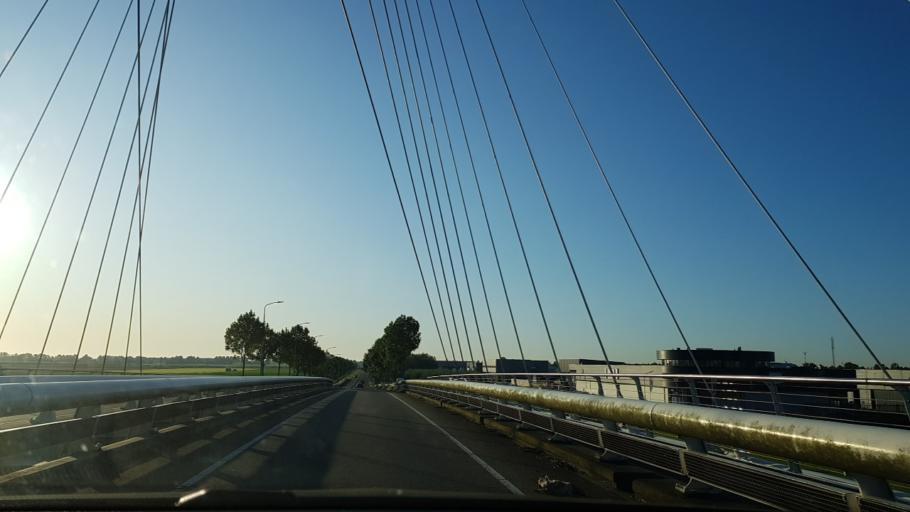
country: NL
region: North Holland
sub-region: Gemeente Haarlemmermeer
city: Hoofddorp
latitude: 52.2729
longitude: 4.6454
